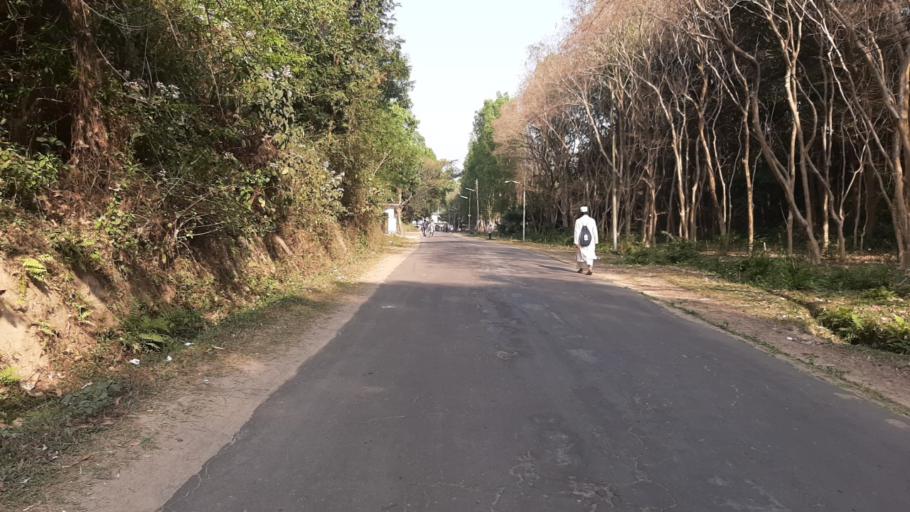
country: BD
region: Chittagong
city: Chittagong
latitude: 22.4743
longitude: 91.7907
